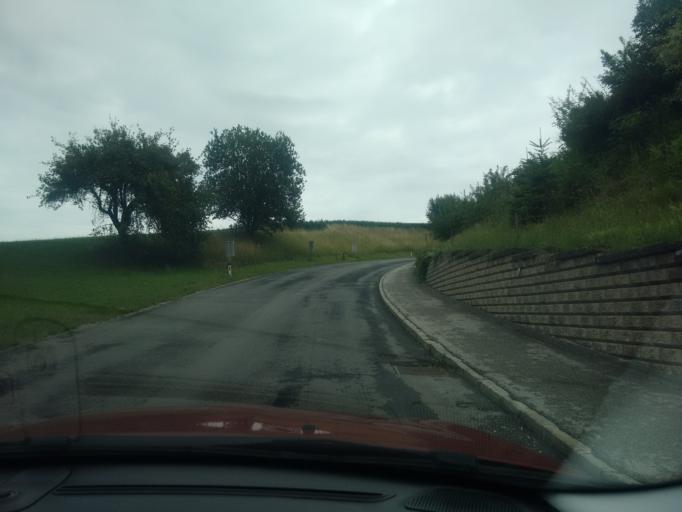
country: AT
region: Upper Austria
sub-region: Politischer Bezirk Steyr-Land
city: Bad Hall
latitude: 48.0397
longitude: 14.2200
